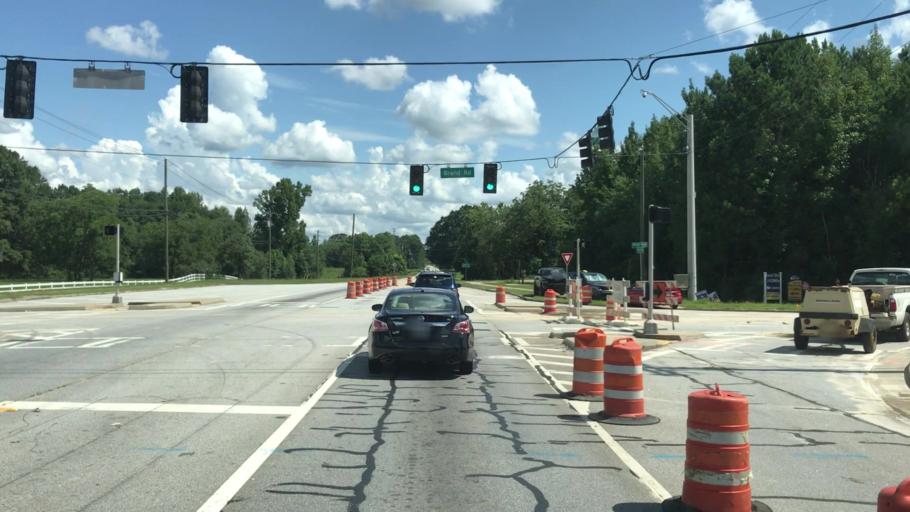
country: US
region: Georgia
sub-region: Walton County
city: Loganville
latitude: 33.8554
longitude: -83.9049
